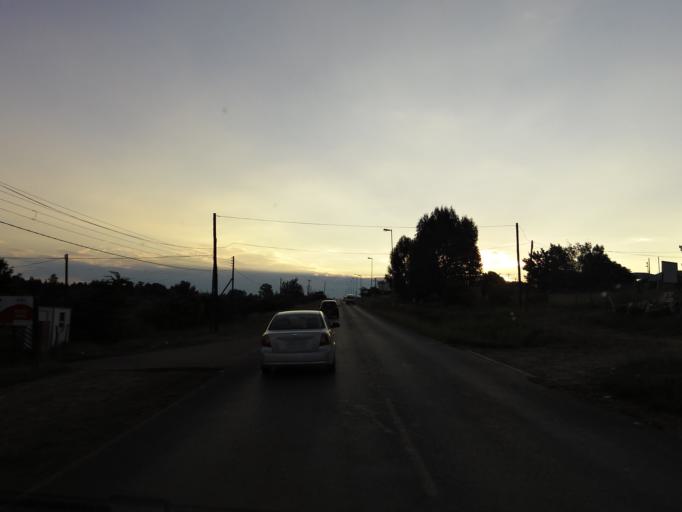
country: LS
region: Leribe
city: Leribe
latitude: -28.8678
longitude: 28.0628
